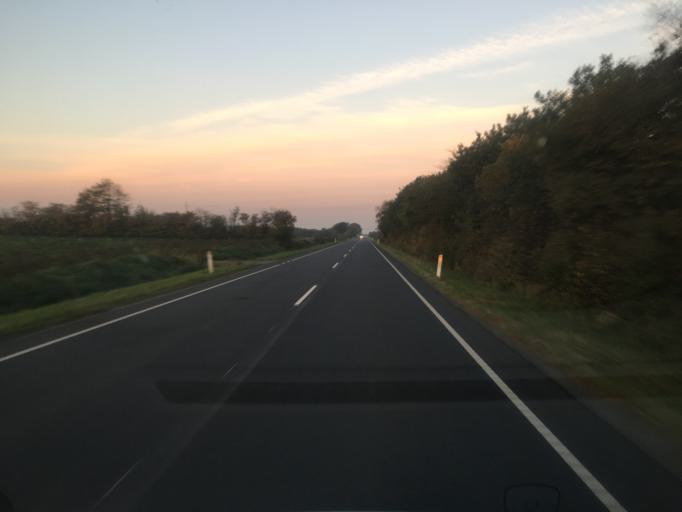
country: DE
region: Schleswig-Holstein
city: Bramstedtlund
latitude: 54.9725
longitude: 9.1054
